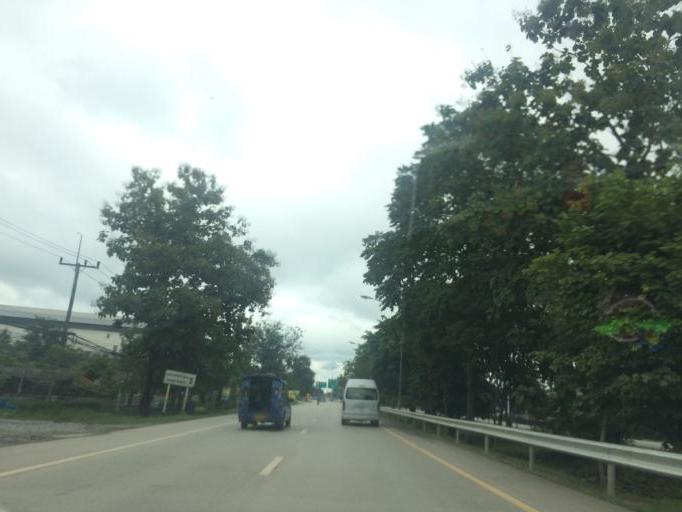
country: TH
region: Chiang Rai
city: Chiang Rai
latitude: 19.8470
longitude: 99.8049
